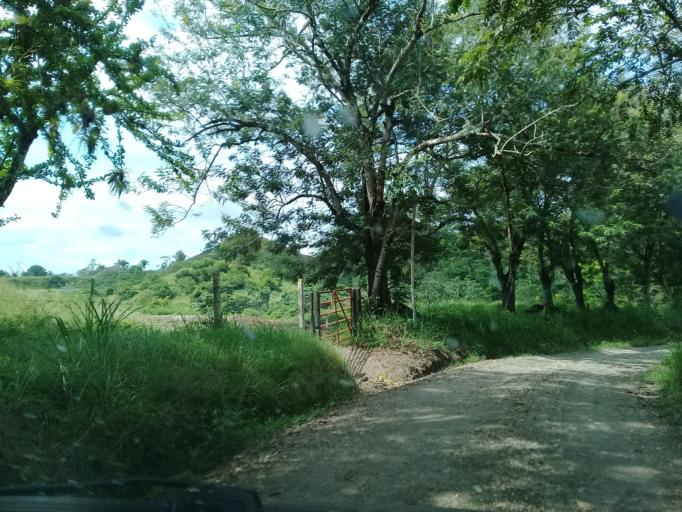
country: CO
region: Antioquia
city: Puerto Triunfo
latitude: 5.6954
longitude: -74.5523
